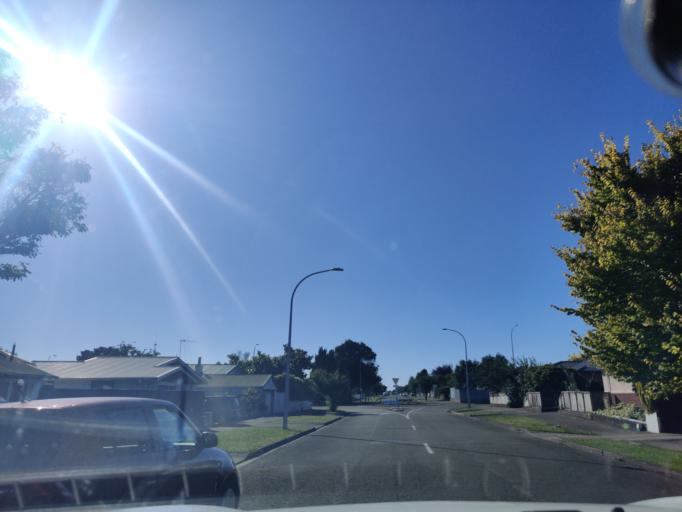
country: NZ
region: Manawatu-Wanganui
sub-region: Palmerston North City
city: Palmerston North
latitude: -40.3605
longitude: 175.5984
